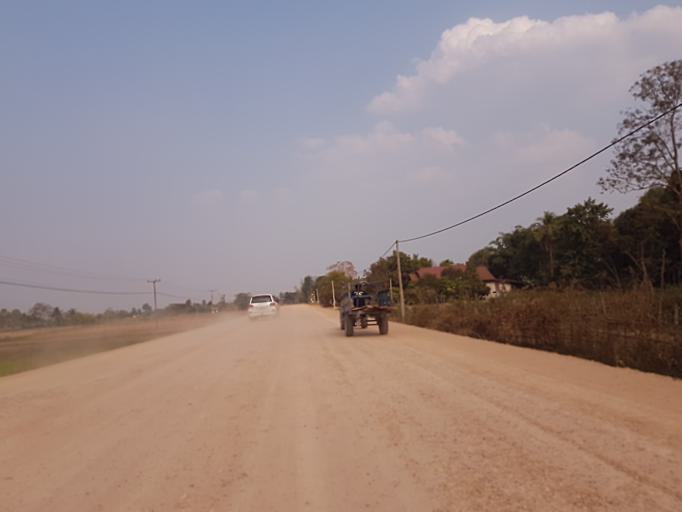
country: TH
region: Nong Khai
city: Nong Khai
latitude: 17.9811
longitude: 102.8830
